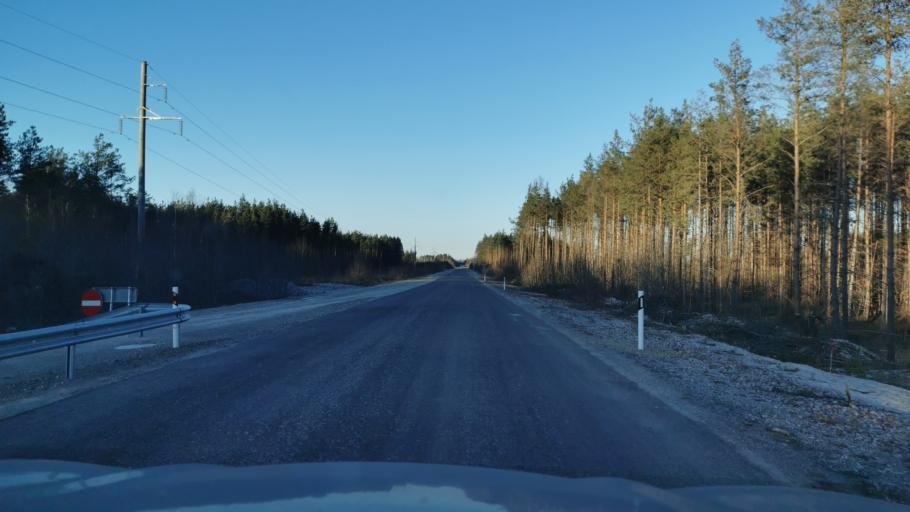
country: EE
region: Ida-Virumaa
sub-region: Puessi linn
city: Pussi
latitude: 59.3366
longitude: 27.0952
